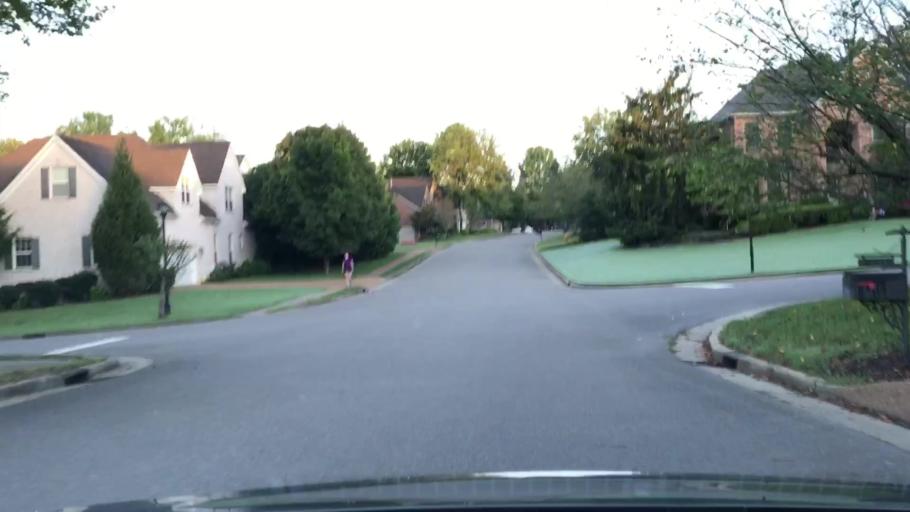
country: US
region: Tennessee
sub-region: Williamson County
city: Brentwood Estates
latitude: 36.0173
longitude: -86.7355
